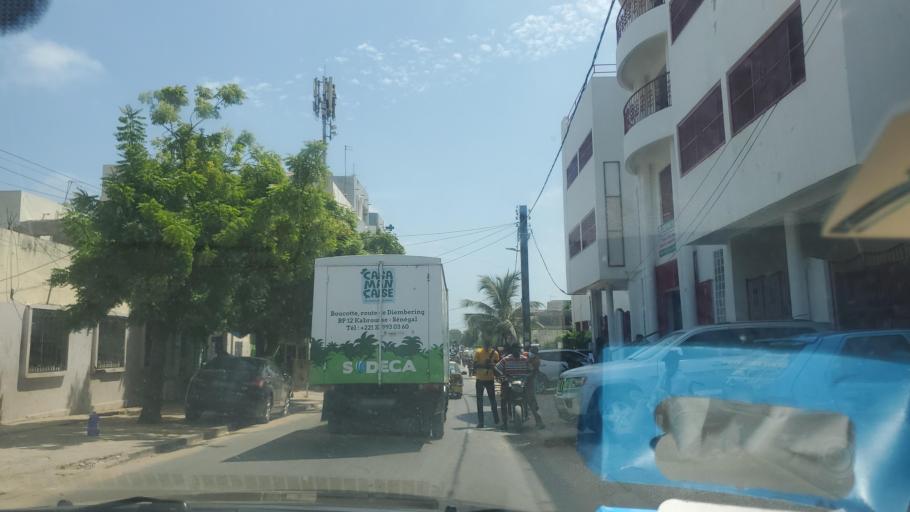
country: SN
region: Dakar
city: Grand Dakar
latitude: 14.7261
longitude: -17.4509
